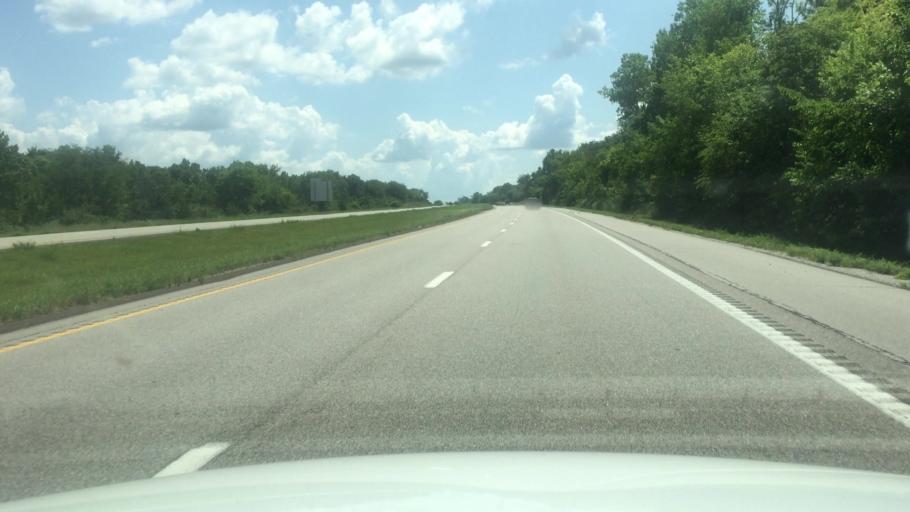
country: US
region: Missouri
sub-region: Platte County
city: Platte City
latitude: 39.2958
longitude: -94.7646
